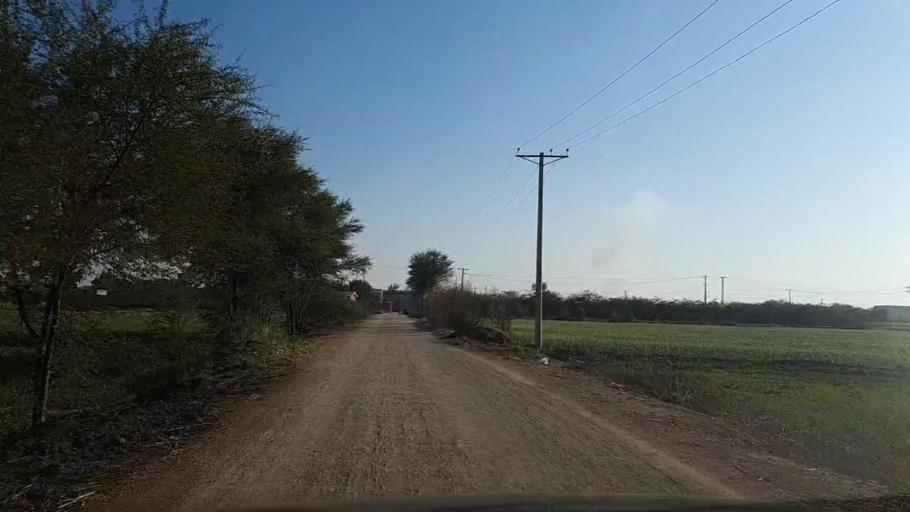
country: PK
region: Sindh
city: Nawabshah
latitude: 26.2055
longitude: 68.3752
